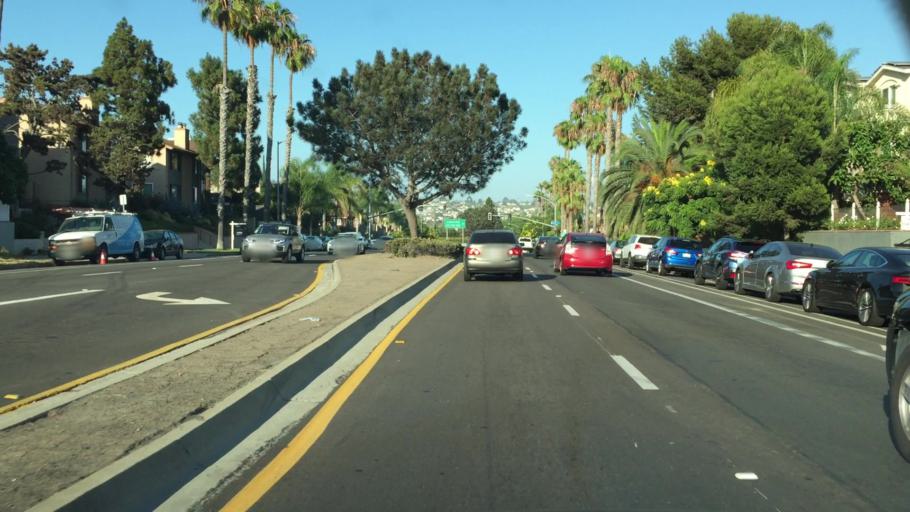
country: US
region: California
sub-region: San Diego County
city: La Jolla
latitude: 32.7999
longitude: -117.2309
